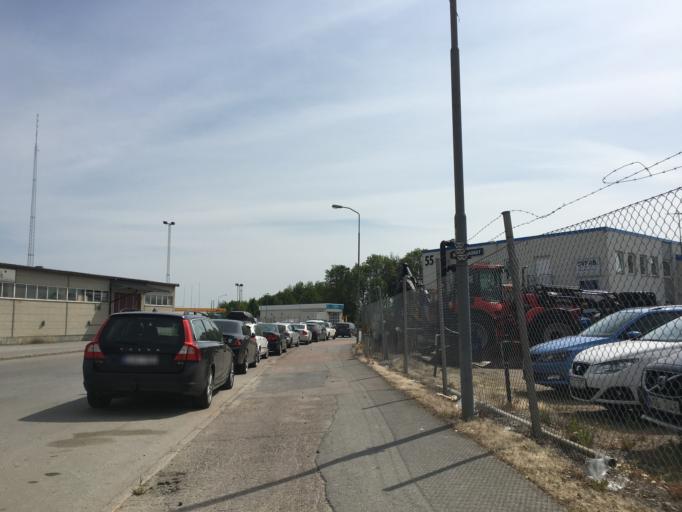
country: SE
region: Uppsala
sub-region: Uppsala Kommun
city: Uppsala
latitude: 59.8478
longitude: 17.6744
